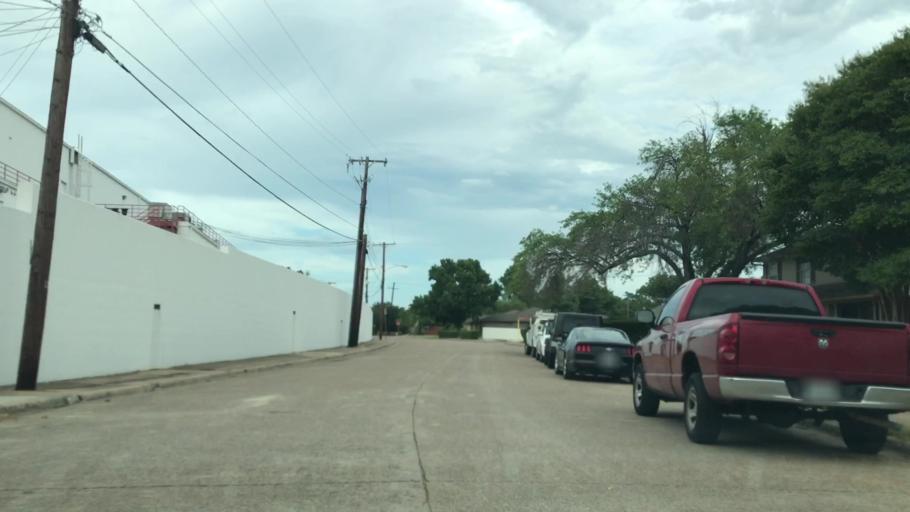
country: US
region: Texas
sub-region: Dallas County
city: Highland Park
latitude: 32.8356
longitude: -96.7758
